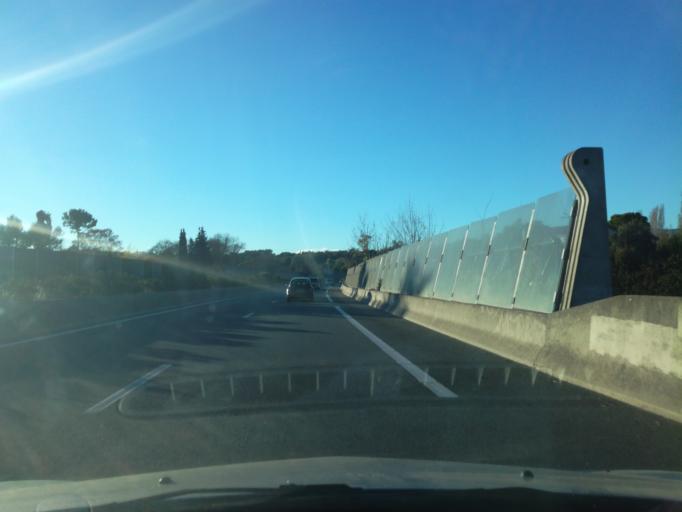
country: FR
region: Provence-Alpes-Cote d'Azur
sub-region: Departement des Alpes-Maritimes
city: Mouans-Sartoux
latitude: 43.6078
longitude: 6.9793
